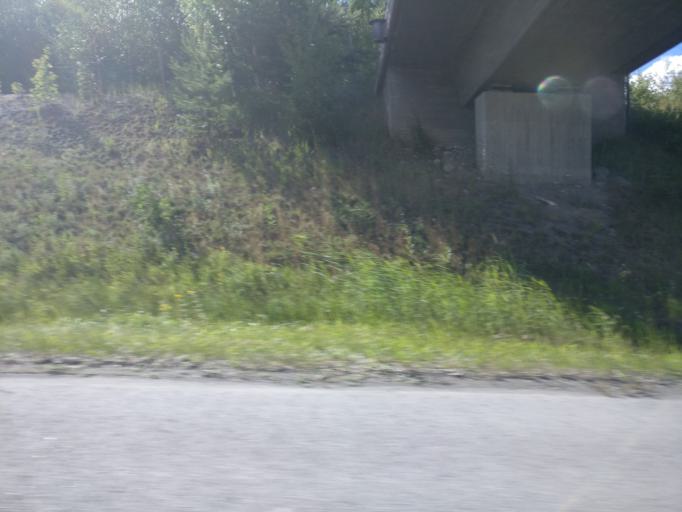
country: FI
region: Paijanne Tavastia
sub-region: Lahti
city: Heinola
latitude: 61.1649
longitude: 25.9970
